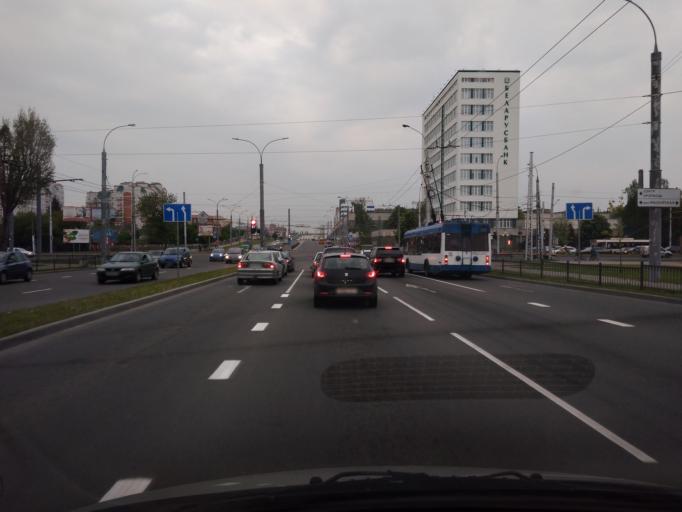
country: BY
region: Brest
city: Brest
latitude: 52.0927
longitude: 23.7329
